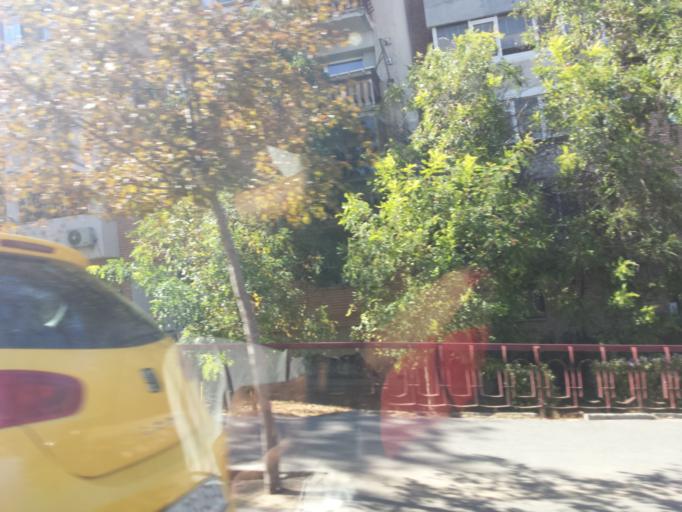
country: RO
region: Tulcea
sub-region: Municipiul Tulcea
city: Tulcea
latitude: 45.1739
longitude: 28.7992
